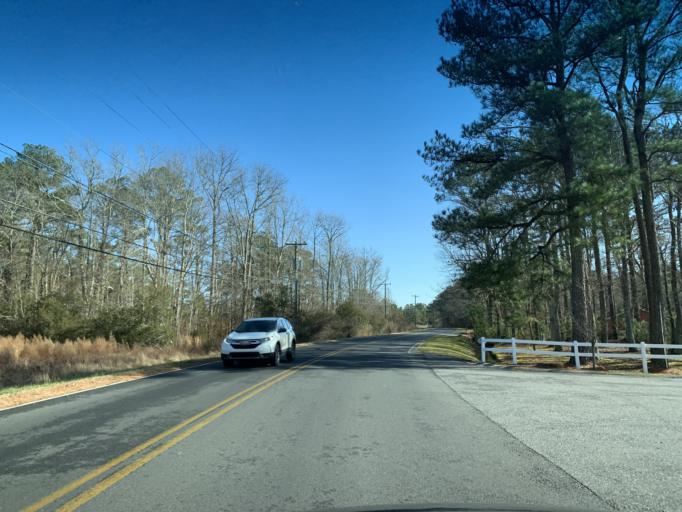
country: US
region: Maryland
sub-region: Worcester County
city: Ocean Pines
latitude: 38.4160
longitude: -75.1217
